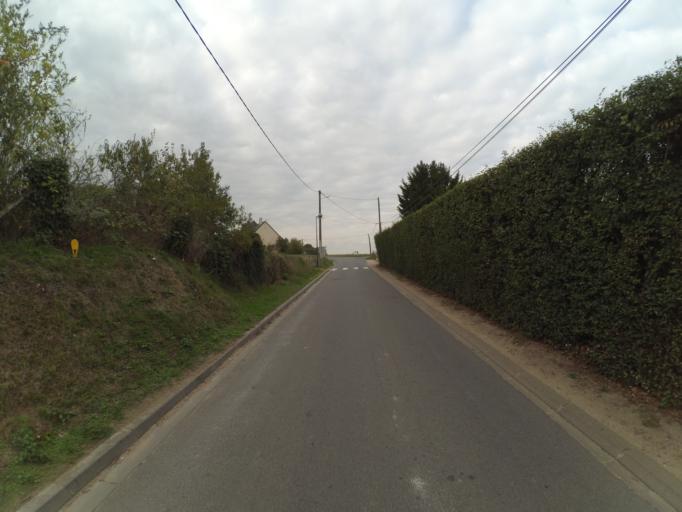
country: FR
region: Centre
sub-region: Departement d'Indre-et-Loire
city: Nazelles-Negron
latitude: 47.4871
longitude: 0.9463
